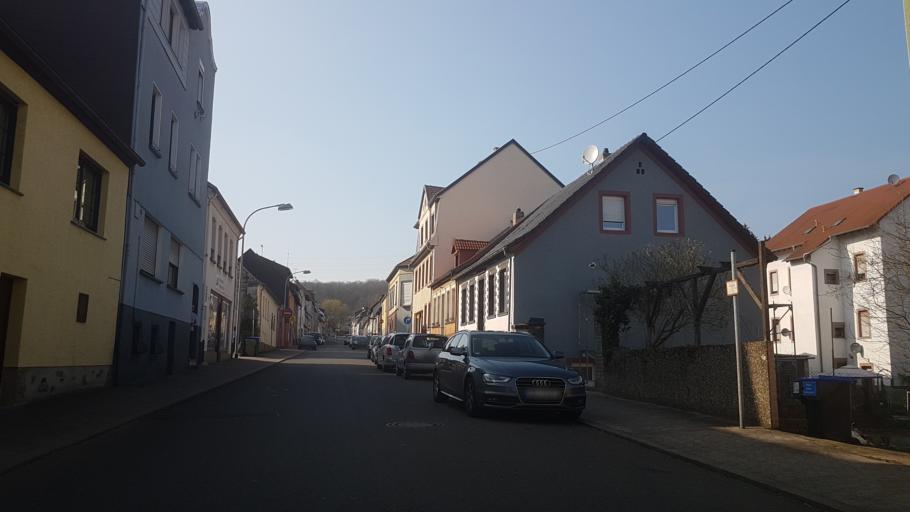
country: DE
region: Saarland
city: Sulzbach
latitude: 49.2728
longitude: 7.0148
